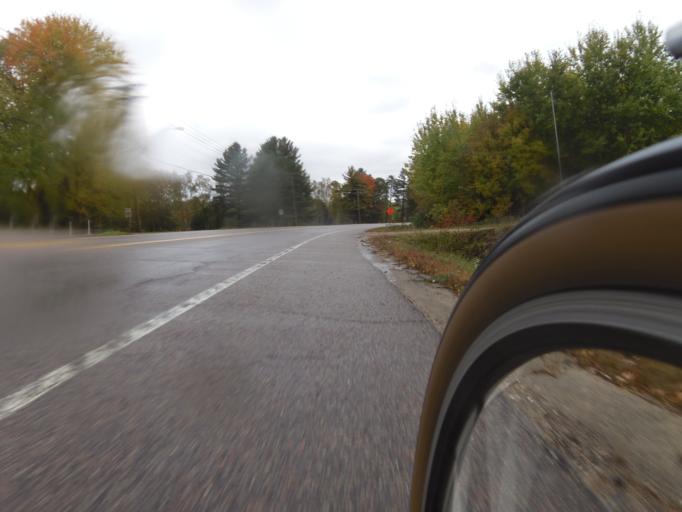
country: CA
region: Quebec
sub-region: Outaouais
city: Fort-Coulonge
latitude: 45.8553
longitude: -76.7386
